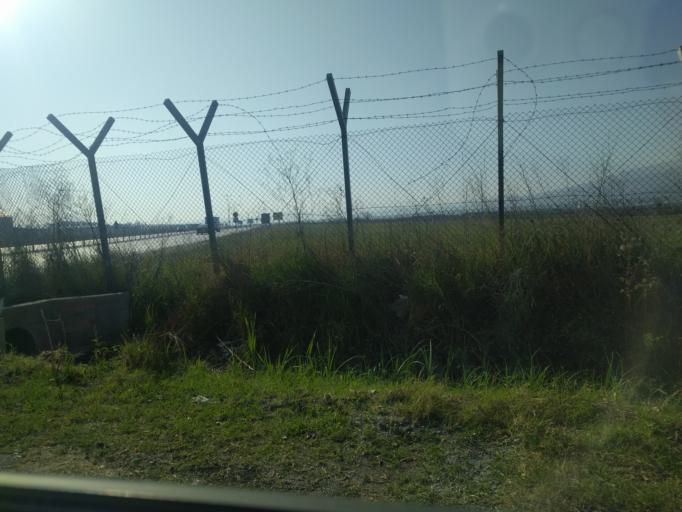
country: XK
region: Pristina
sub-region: Komuna e Gracanices
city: Glanica
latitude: 42.5833
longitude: 21.0269
